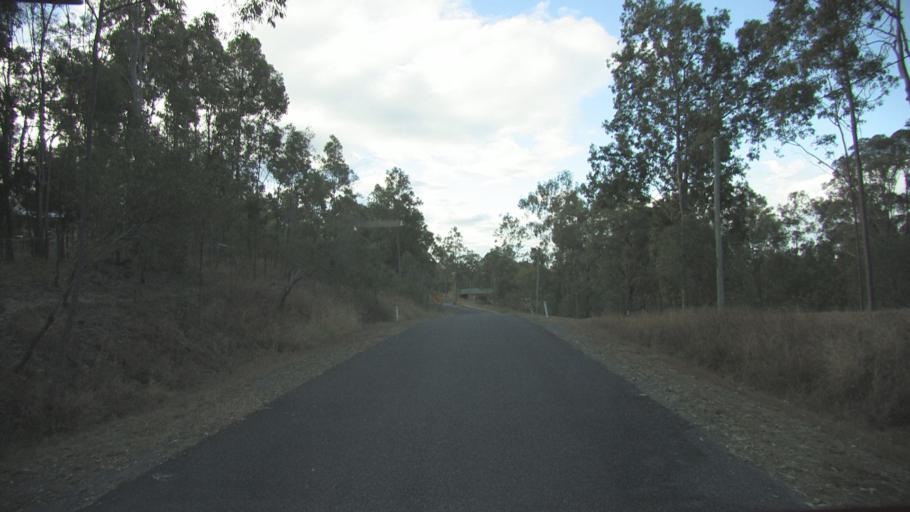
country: AU
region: Queensland
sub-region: Logan
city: Cedar Vale
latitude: -27.9036
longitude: 153.0734
